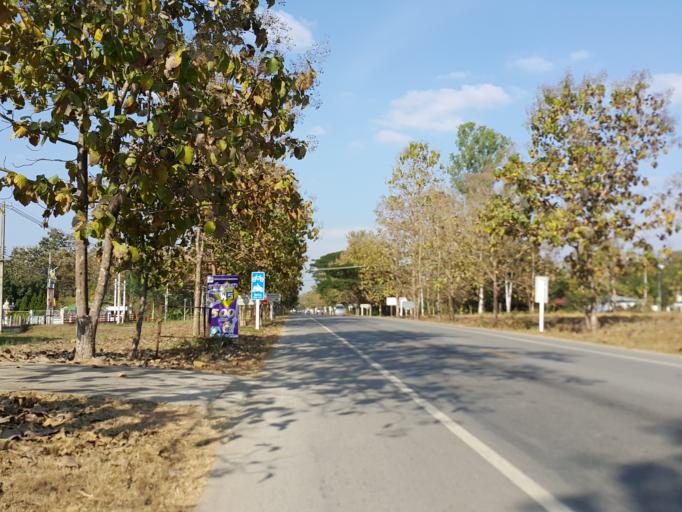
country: TH
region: Chiang Mai
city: Mae On
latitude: 18.7900
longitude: 99.2433
